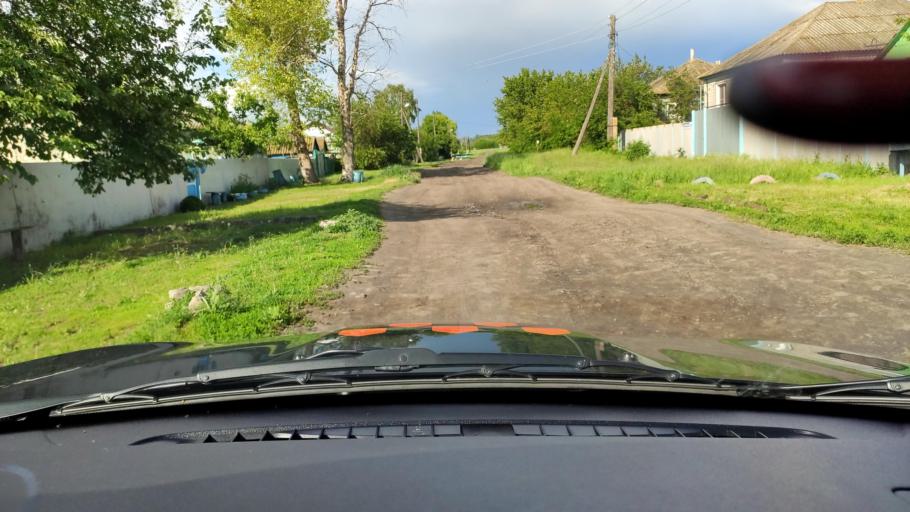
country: RU
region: Voronezj
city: Uryv-Pokrovka
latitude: 51.1145
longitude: 39.1797
